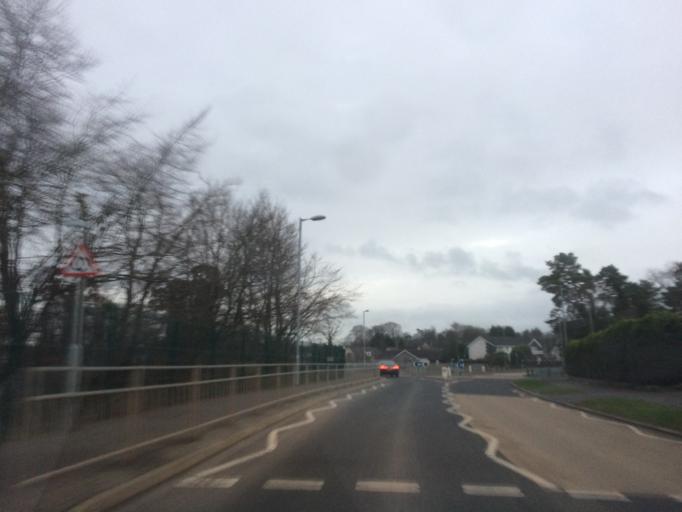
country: GB
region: Scotland
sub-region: East Renfrewshire
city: Newton Mearns
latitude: 55.7859
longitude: -4.3289
